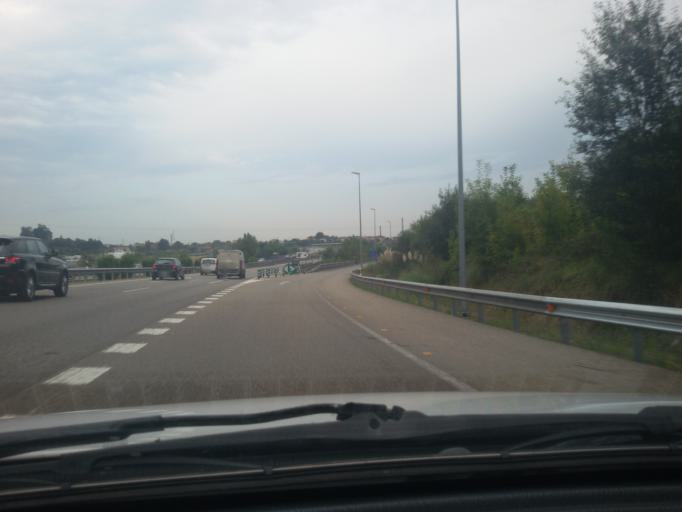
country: ES
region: Asturias
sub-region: Province of Asturias
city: Lugones
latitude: 43.3974
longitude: -5.8229
